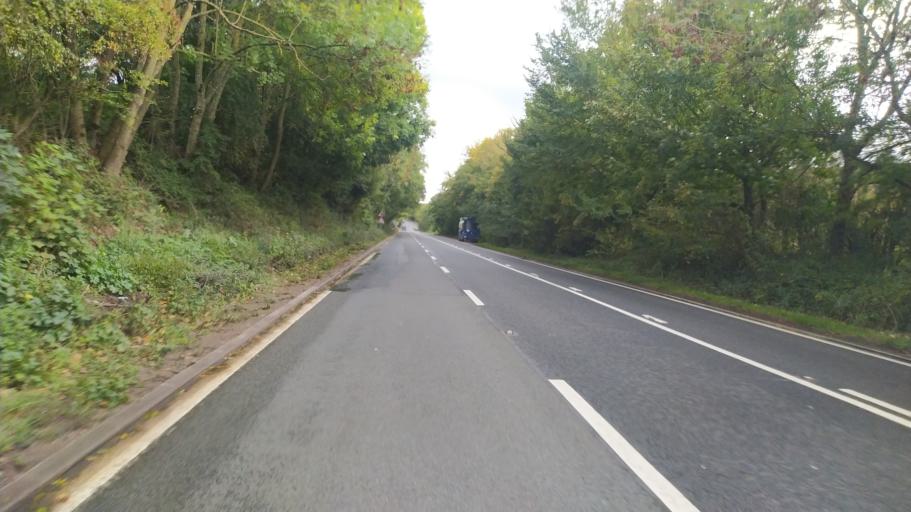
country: GB
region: England
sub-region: Dorset
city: Bridport
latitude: 50.7345
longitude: -2.7261
